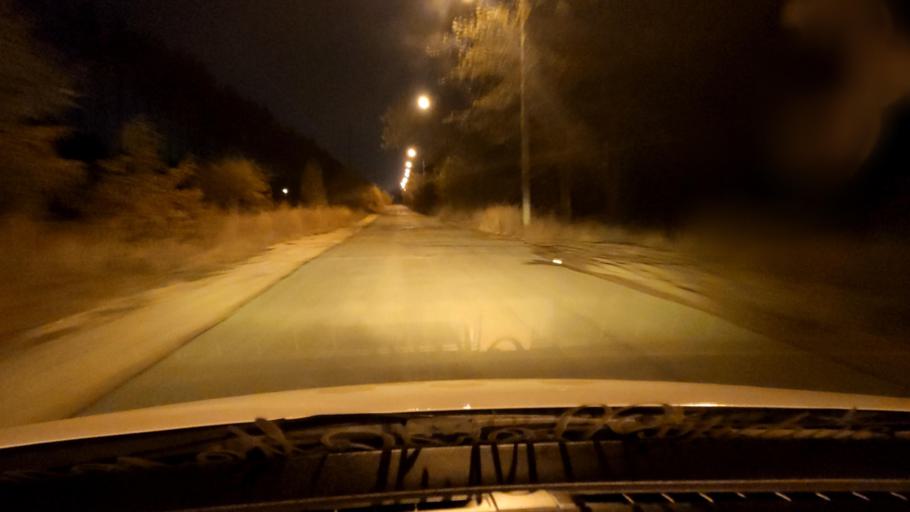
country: RU
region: Voronezj
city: Pridonskoy
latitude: 51.6850
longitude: 39.0914
